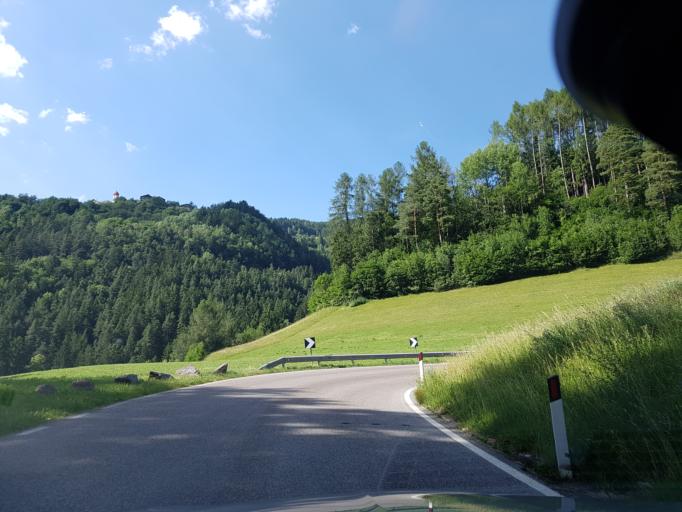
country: IT
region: Trentino-Alto Adige
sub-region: Bolzano
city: Laion
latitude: 46.5958
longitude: 11.6137
